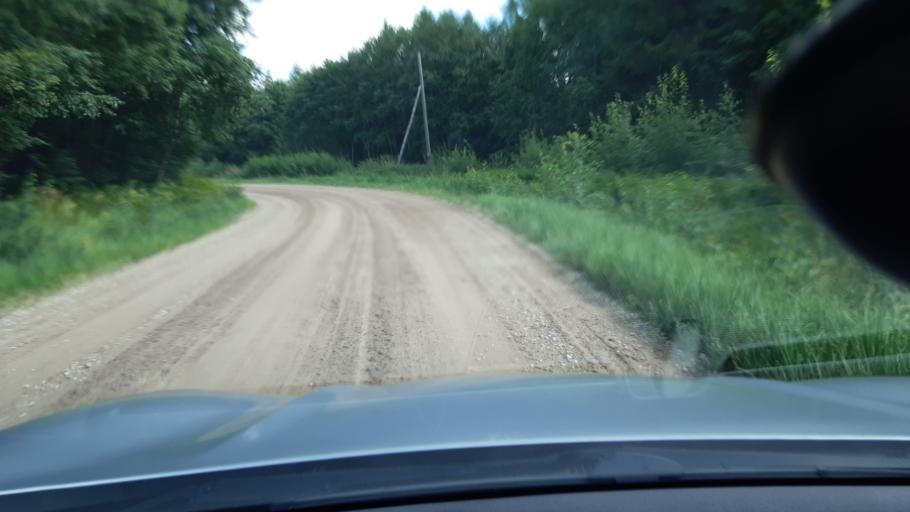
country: EE
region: Jaervamaa
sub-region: Tueri vald
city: Tueri
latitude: 58.9258
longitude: 25.2138
